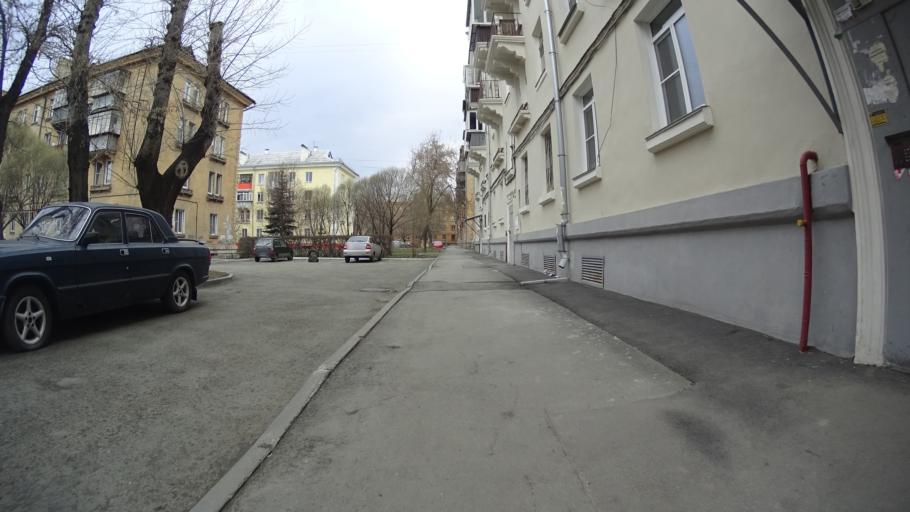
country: RU
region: Chelyabinsk
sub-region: Gorod Chelyabinsk
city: Chelyabinsk
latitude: 55.1629
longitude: 61.4408
